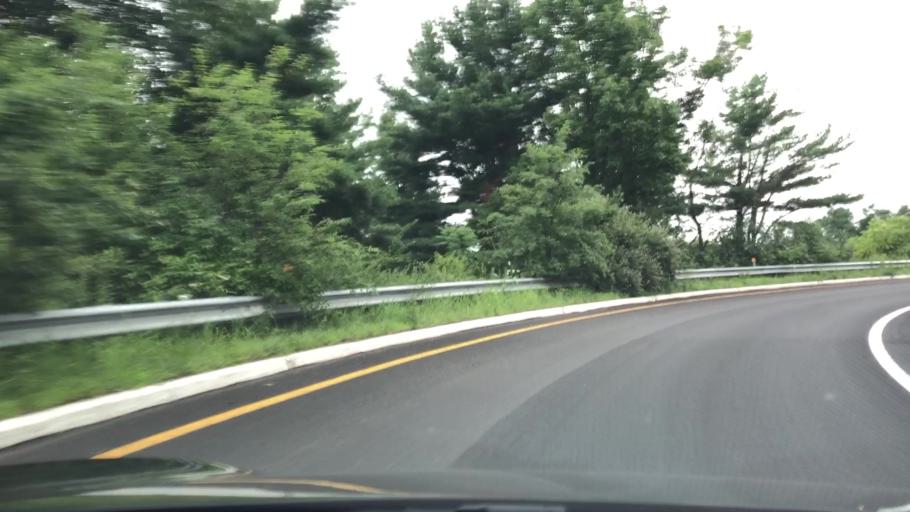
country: US
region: New Jersey
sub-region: Mercer County
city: Lawrenceville
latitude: 40.2832
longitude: -74.6943
